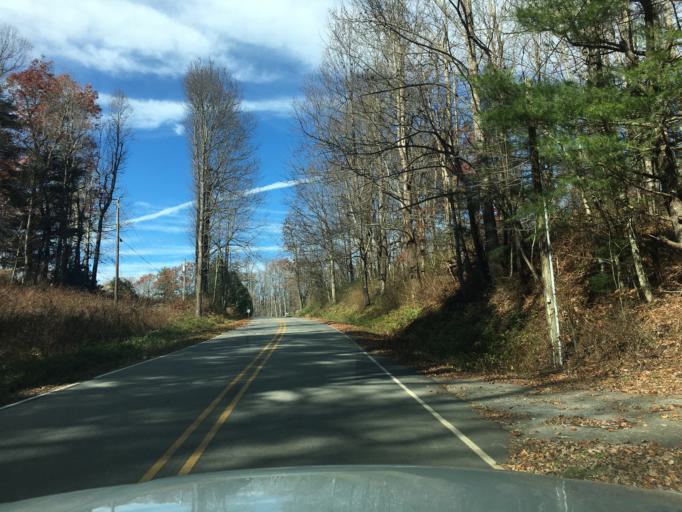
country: US
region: North Carolina
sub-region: Henderson County
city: Valley Hill
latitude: 35.2323
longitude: -82.5105
